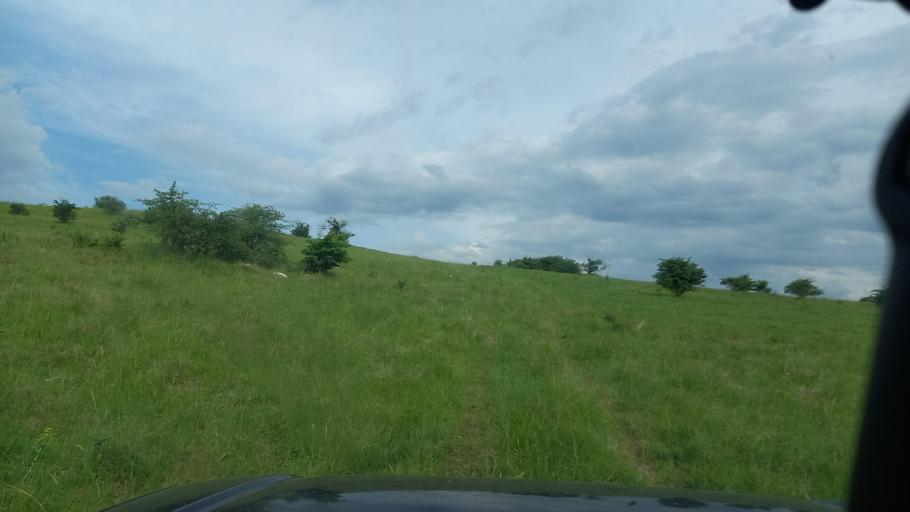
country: RU
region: Karachayevo-Cherkesiya
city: Kurdzhinovo
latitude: 44.1284
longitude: 41.0585
